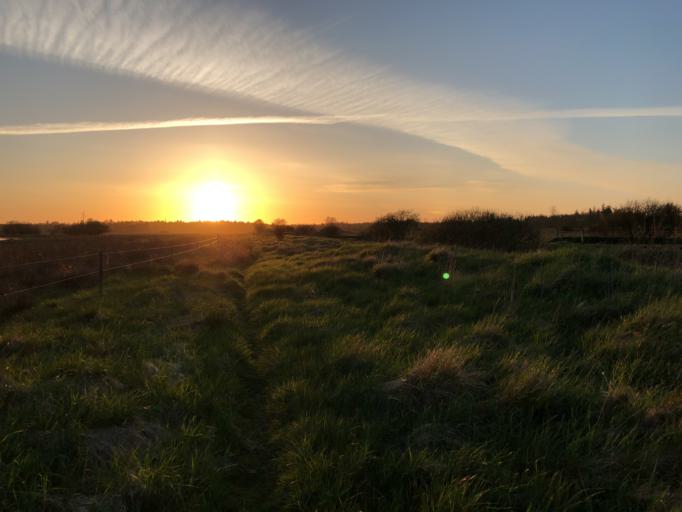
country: DK
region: Central Jutland
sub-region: Holstebro Kommune
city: Ulfborg
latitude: 56.2478
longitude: 8.4100
